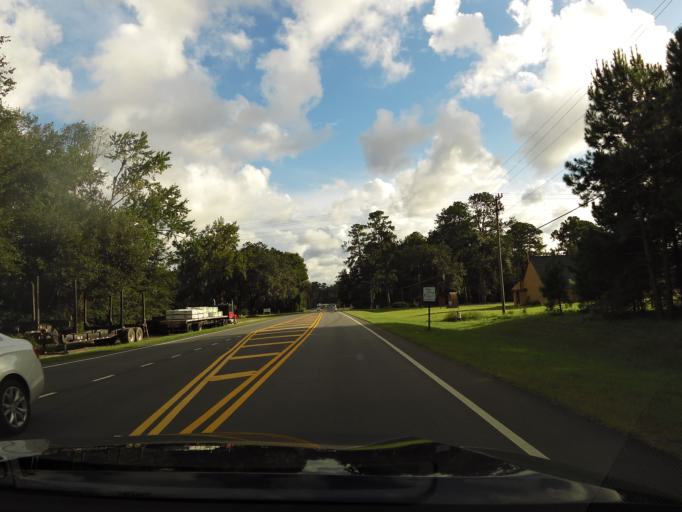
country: US
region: Georgia
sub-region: Liberty County
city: Midway
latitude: 31.8103
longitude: -81.4306
